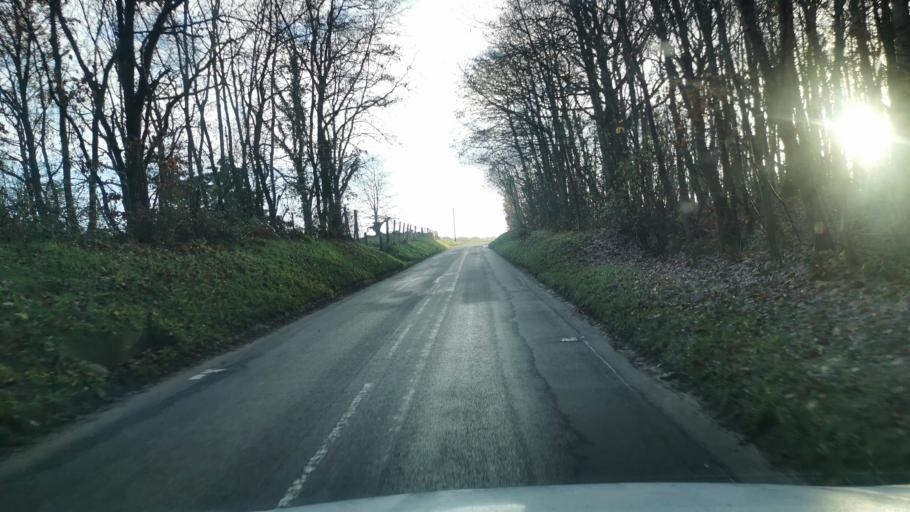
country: FR
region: Ile-de-France
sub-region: Departement des Yvelines
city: Houdan
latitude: 48.8325
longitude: 1.6213
